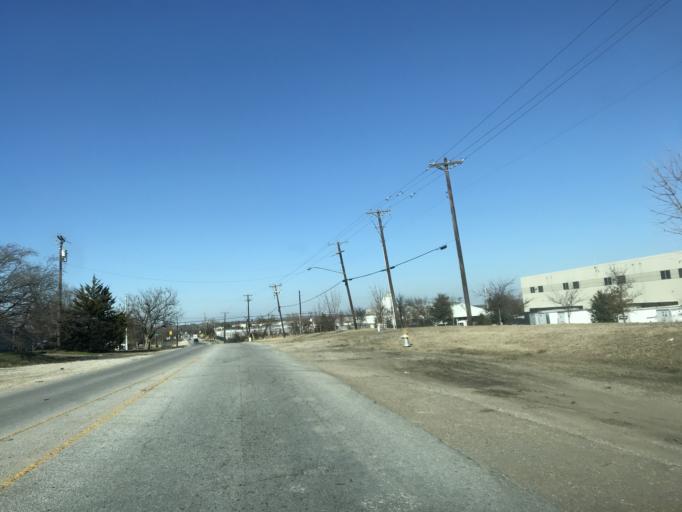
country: US
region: Texas
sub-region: Dallas County
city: Cockrell Hill
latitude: 32.7679
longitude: -96.9025
